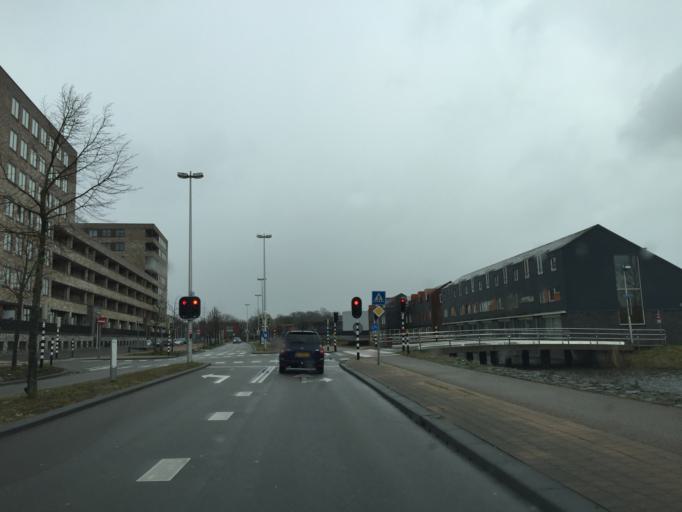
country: NL
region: Utrecht
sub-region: Stichtse Vecht
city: Maarssen
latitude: 52.0857
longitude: 5.0628
